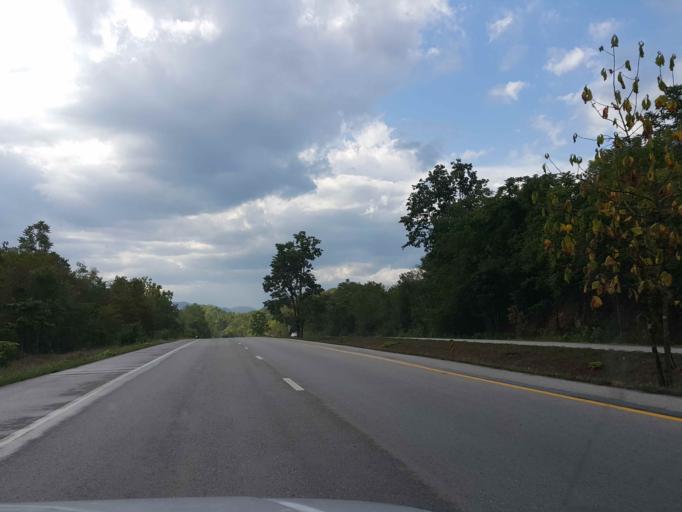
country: TH
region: Lampang
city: Thoen
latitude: 17.6803
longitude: 99.2412
